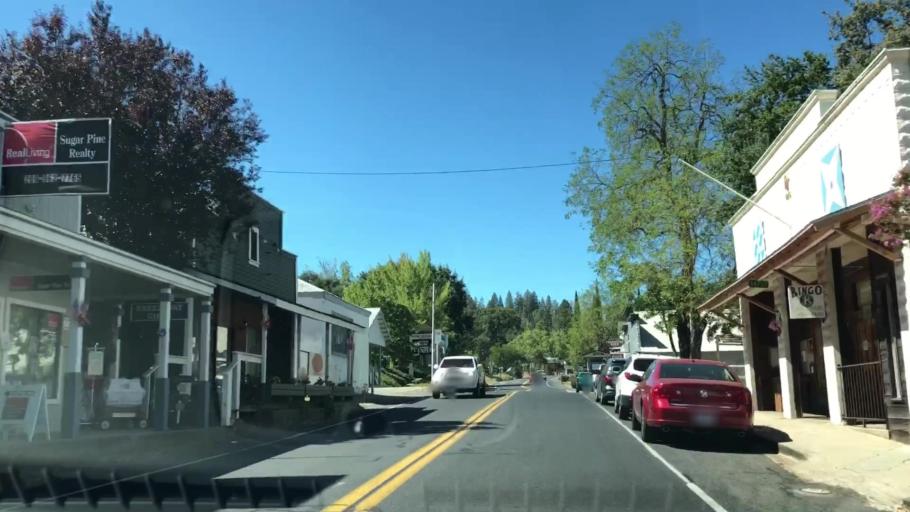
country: US
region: California
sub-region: Tuolumne County
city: Tuolumne City
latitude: 37.8389
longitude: -120.2306
